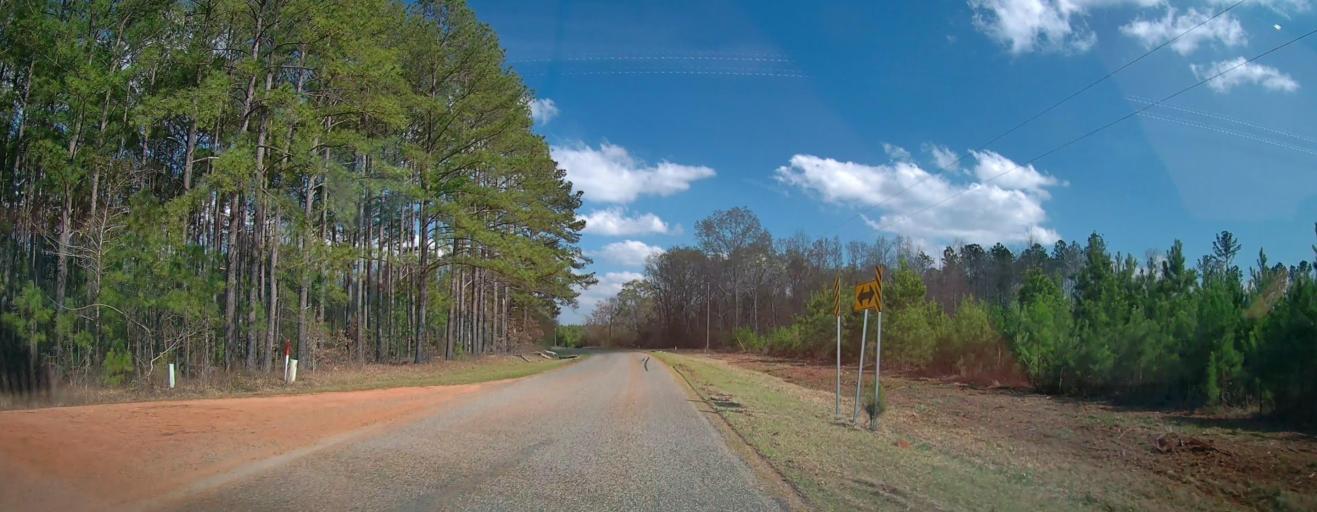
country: US
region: Georgia
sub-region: Wilkinson County
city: Irwinton
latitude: 32.6402
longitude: -83.1681
